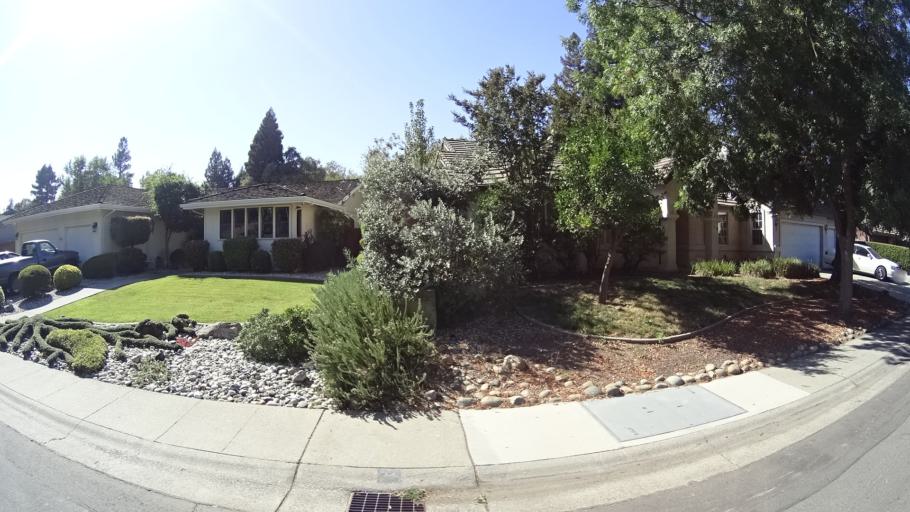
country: US
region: California
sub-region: Sacramento County
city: Parkway
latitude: 38.4790
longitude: -121.5154
